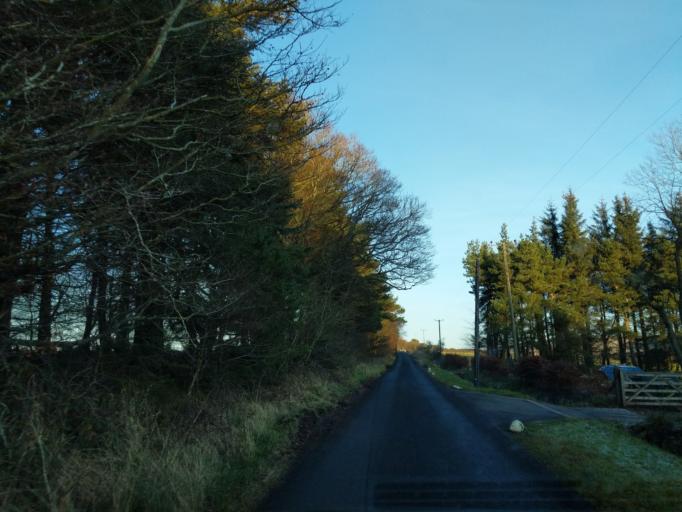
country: GB
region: Scotland
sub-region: Edinburgh
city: Balerno
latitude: 55.8584
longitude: -3.3522
